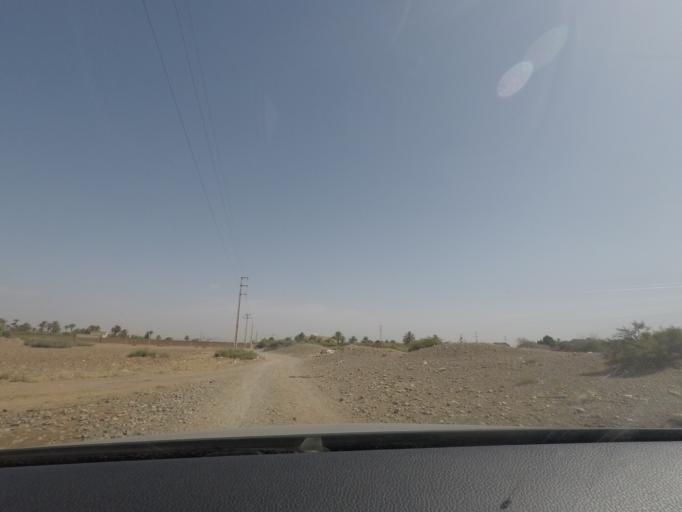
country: MA
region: Marrakech-Tensift-Al Haouz
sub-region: Marrakech
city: Marrakesh
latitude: 31.5780
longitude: -8.0257
